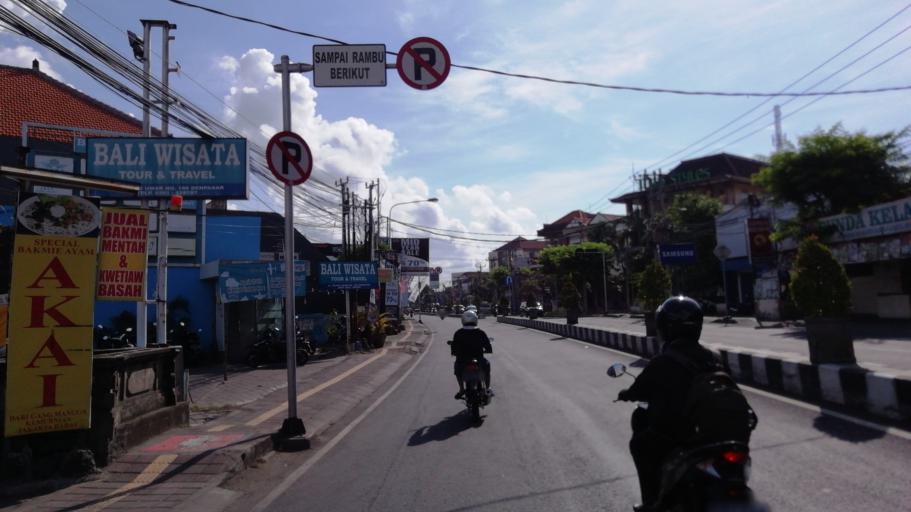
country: ID
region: Bali
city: Karyadharma
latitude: -8.6796
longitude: 115.2042
